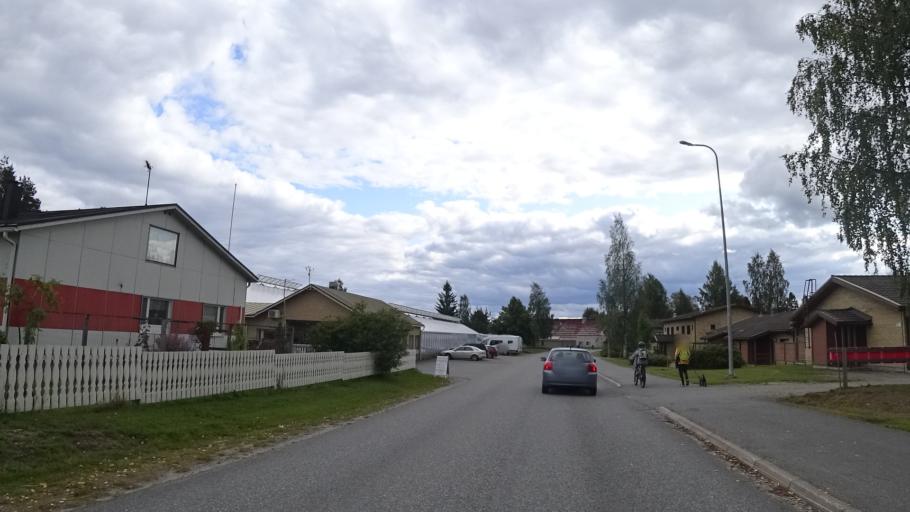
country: FI
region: North Karelia
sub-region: Joensuu
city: Ilomantsi
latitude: 62.6708
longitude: 30.9375
